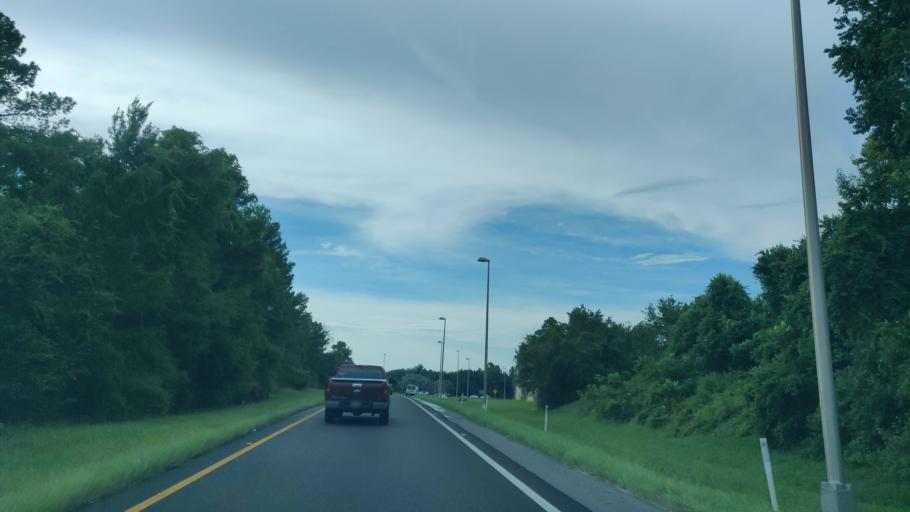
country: US
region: Florida
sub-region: Volusia County
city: Deltona
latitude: 28.9131
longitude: -81.2693
